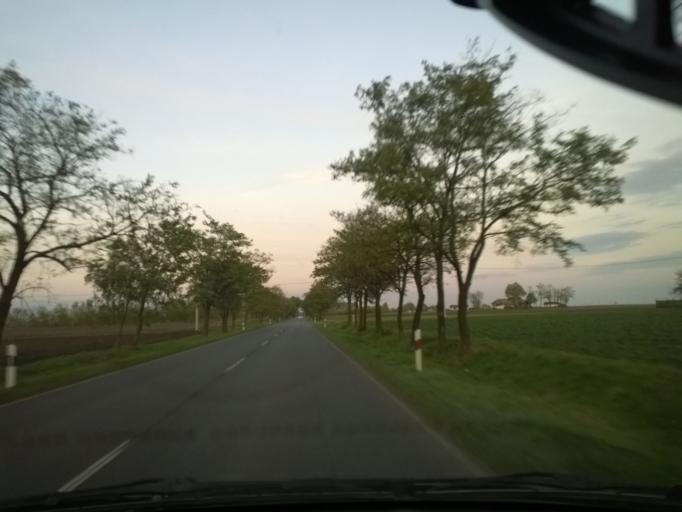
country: HU
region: Csongrad
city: Csongrad
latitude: 46.7112
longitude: 20.0654
